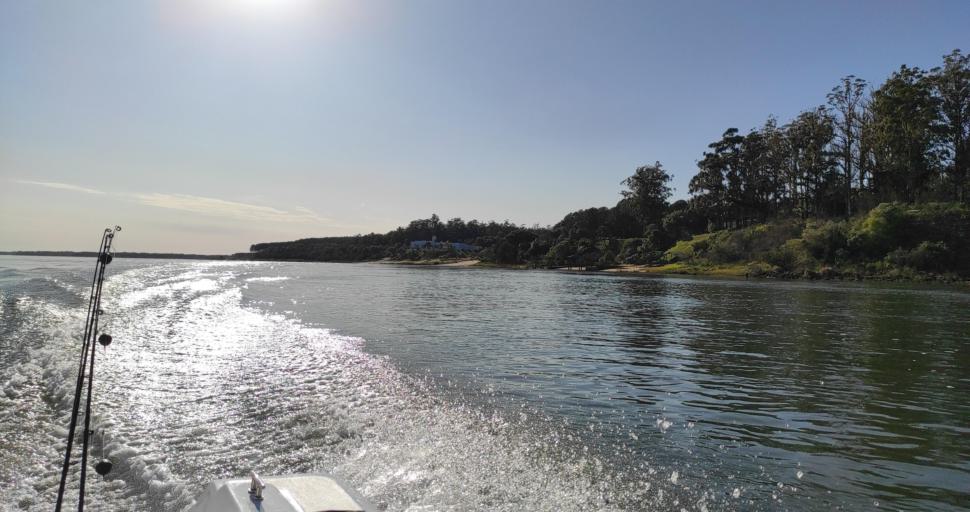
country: AR
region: Corrientes
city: Ituzaingo
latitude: -27.5949
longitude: -56.8101
